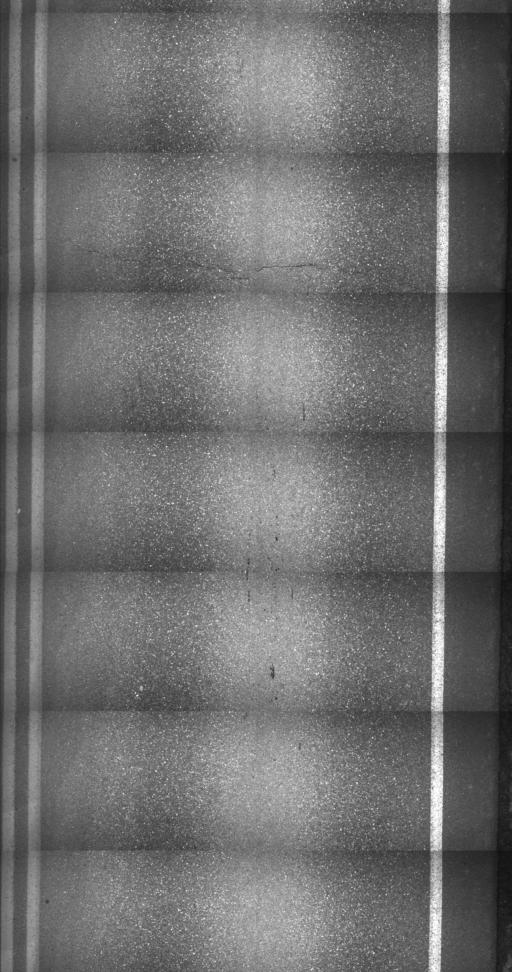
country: US
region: Vermont
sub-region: Chittenden County
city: Colchester
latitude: 44.5429
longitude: -73.1681
